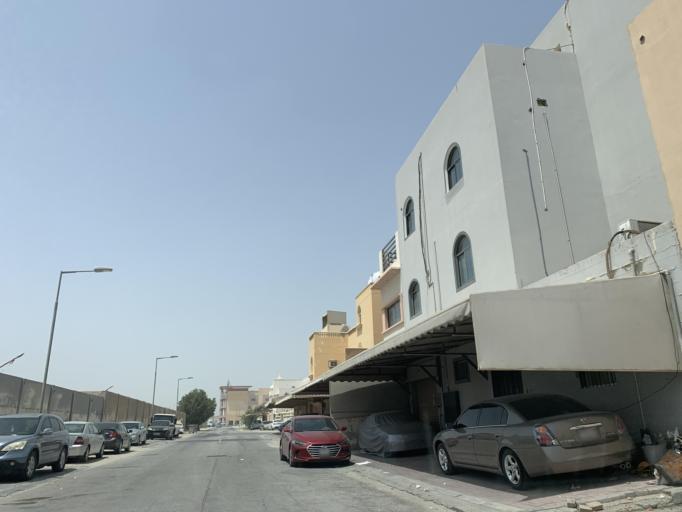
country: BH
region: Northern
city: Madinat `Isa
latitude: 26.1618
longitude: 50.5269
